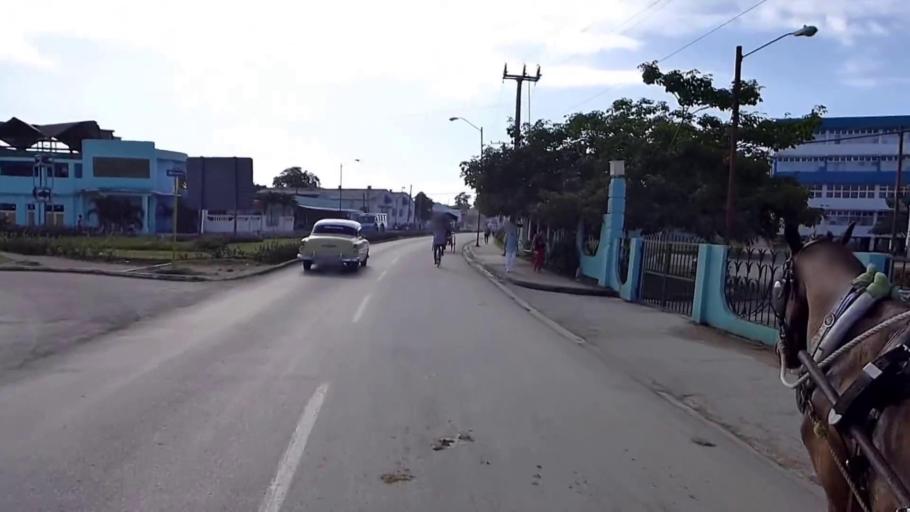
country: CU
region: Camaguey
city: Camaguey
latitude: 21.3840
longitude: -77.9312
